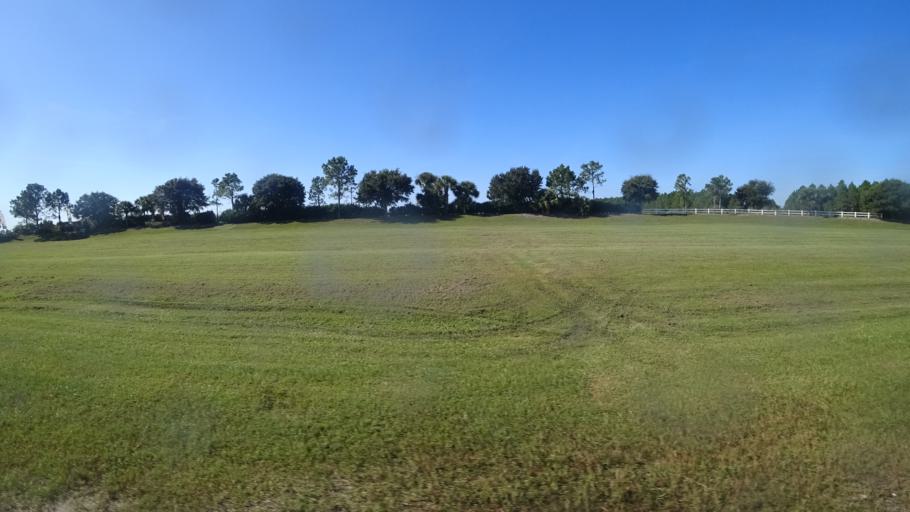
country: US
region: Florida
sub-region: Hillsborough County
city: Wimauma
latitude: 27.6613
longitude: -82.3291
